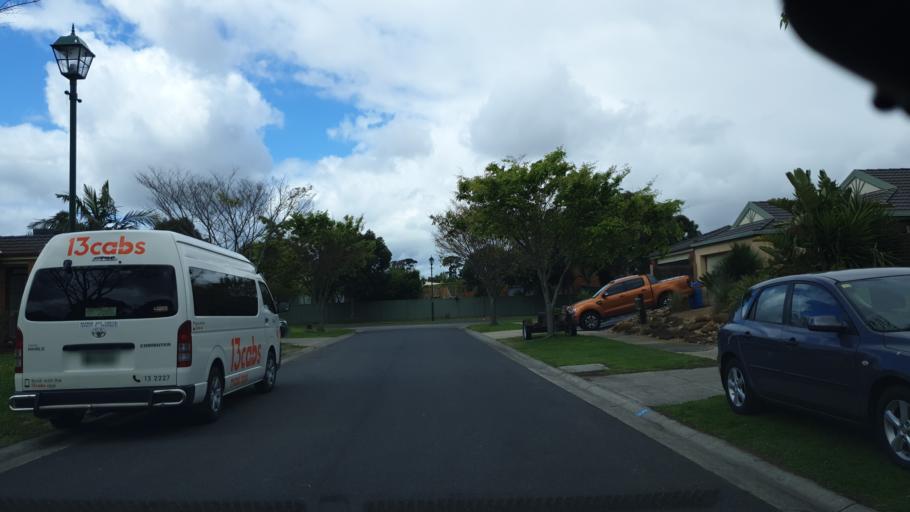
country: AU
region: Victoria
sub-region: Casey
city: Cranbourne East
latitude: -38.1053
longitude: 145.2932
